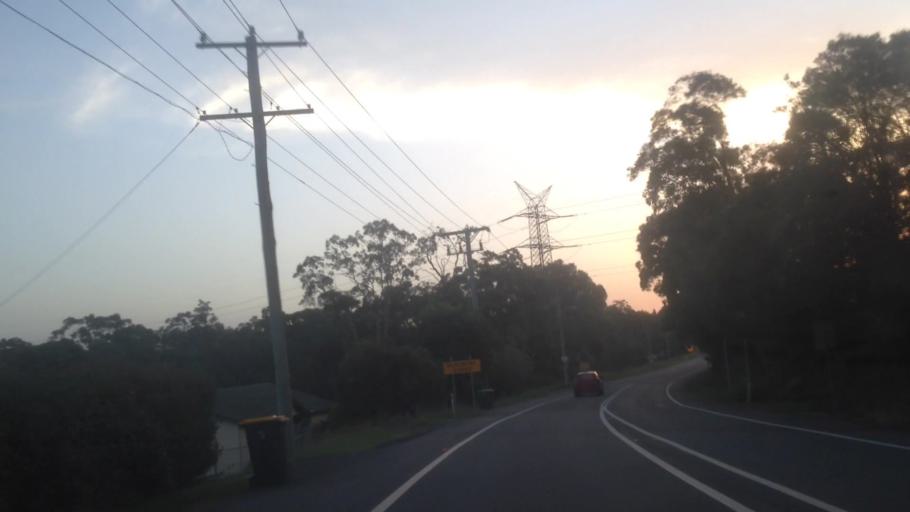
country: AU
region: New South Wales
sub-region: Lake Macquarie Shire
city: Dora Creek
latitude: -33.1044
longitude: 151.5007
